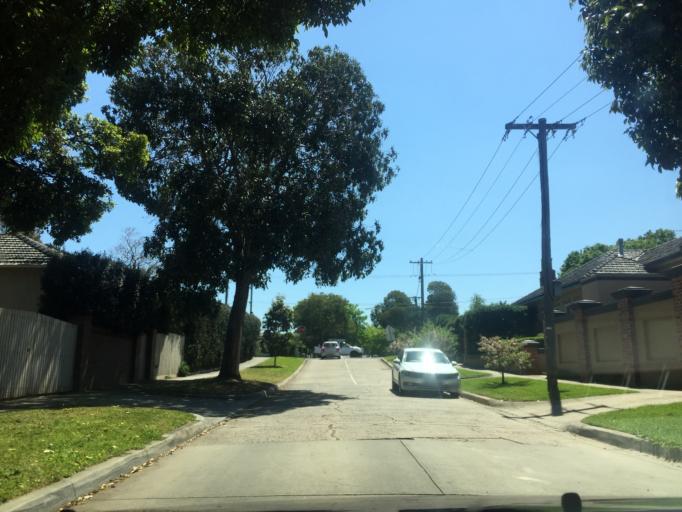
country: AU
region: Victoria
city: Mont Albert
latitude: -37.8150
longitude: 145.0948
